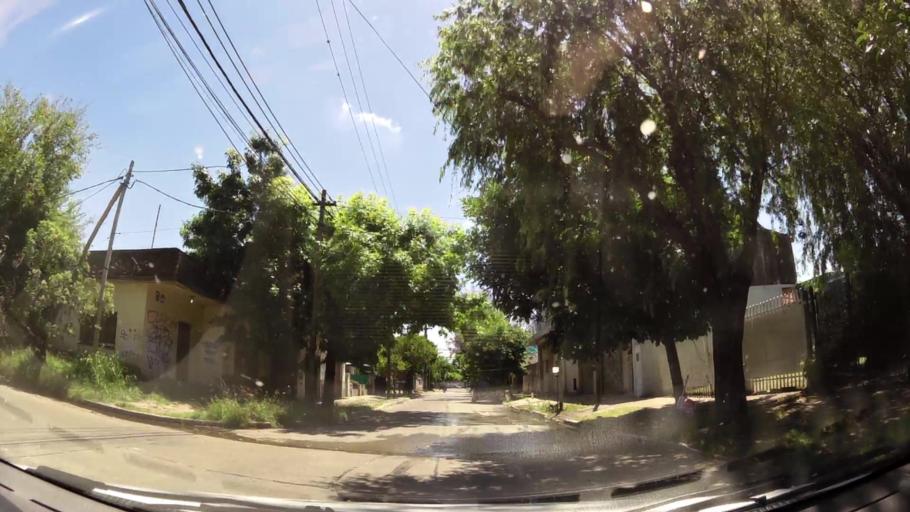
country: AR
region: Buenos Aires
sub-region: Partido de Merlo
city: Merlo
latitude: -34.6581
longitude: -58.7113
